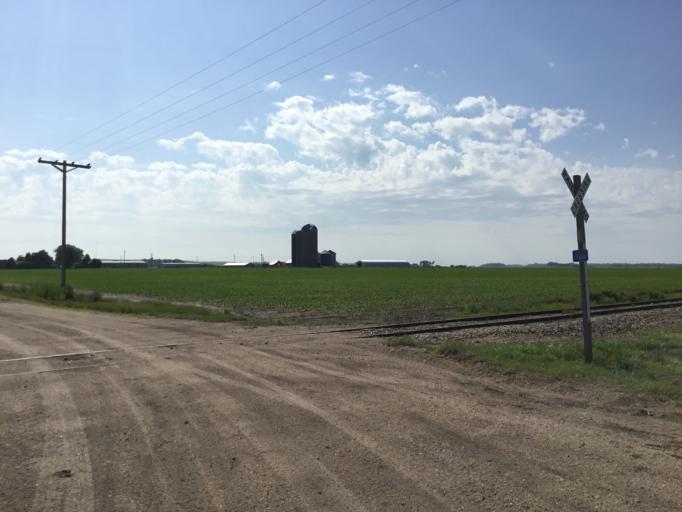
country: US
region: Kansas
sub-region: Cloud County
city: Concordia
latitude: 39.6682
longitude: -97.7704
